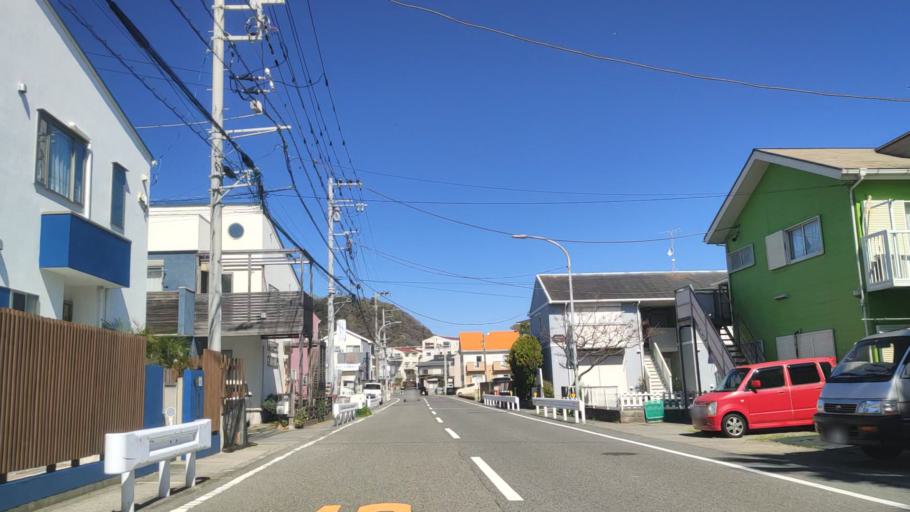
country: JP
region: Kanagawa
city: Hiratsuka
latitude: 35.3148
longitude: 139.3299
